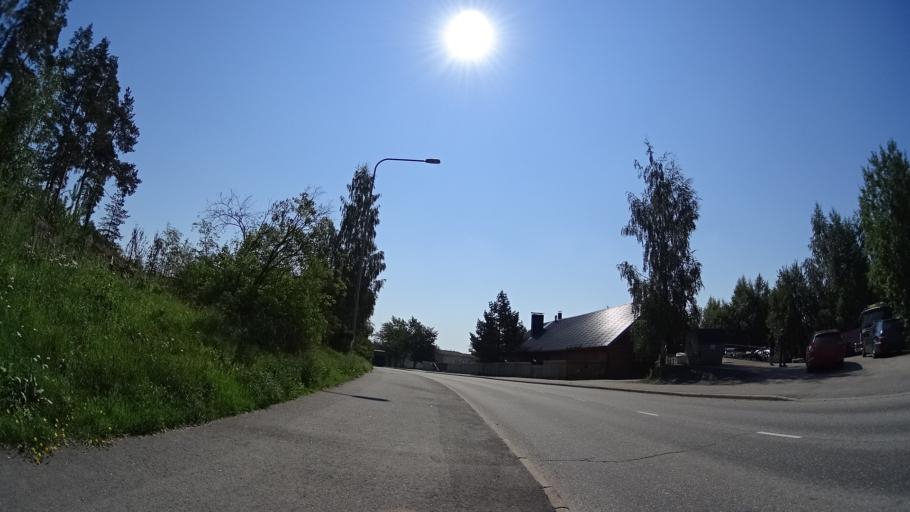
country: FI
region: Uusimaa
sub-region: Helsinki
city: Kerava
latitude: 60.3679
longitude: 25.0759
